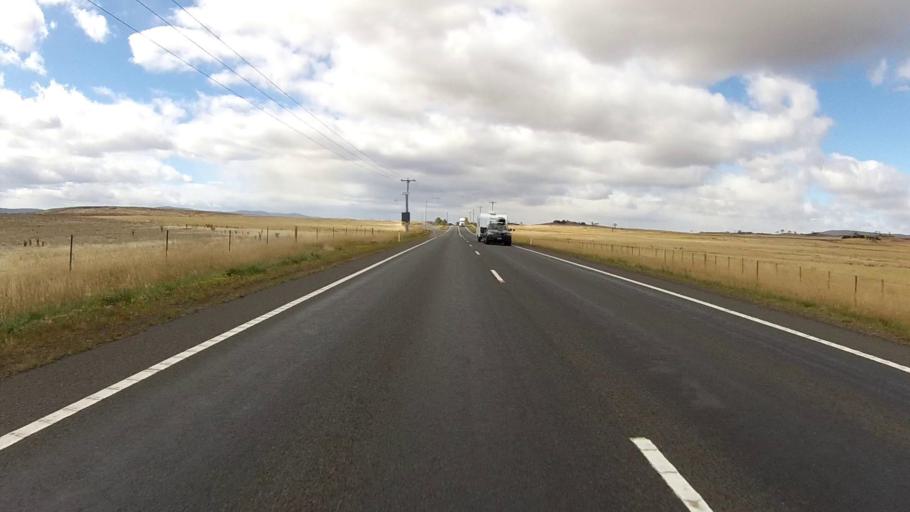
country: AU
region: Tasmania
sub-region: Northern Midlands
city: Evandale
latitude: -41.8811
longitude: 147.4651
